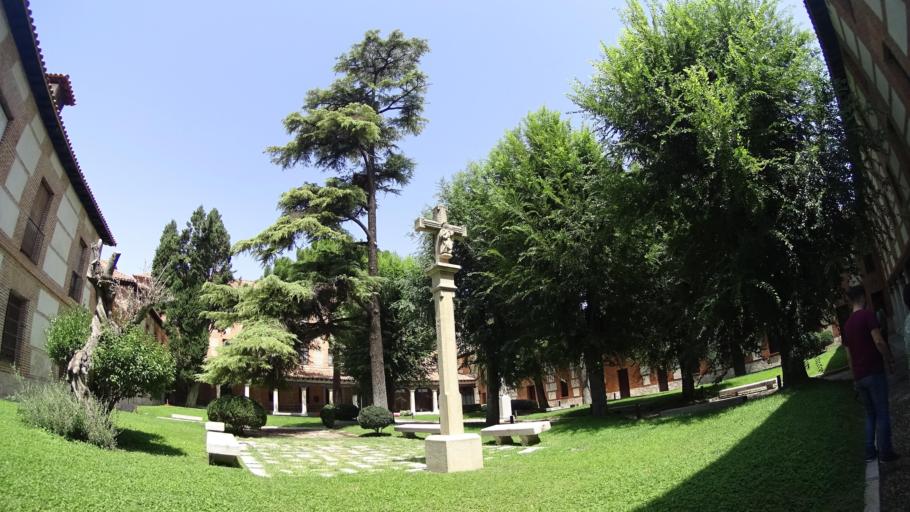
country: ES
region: Madrid
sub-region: Provincia de Madrid
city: Alcala de Henares
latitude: 40.4820
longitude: -3.3627
